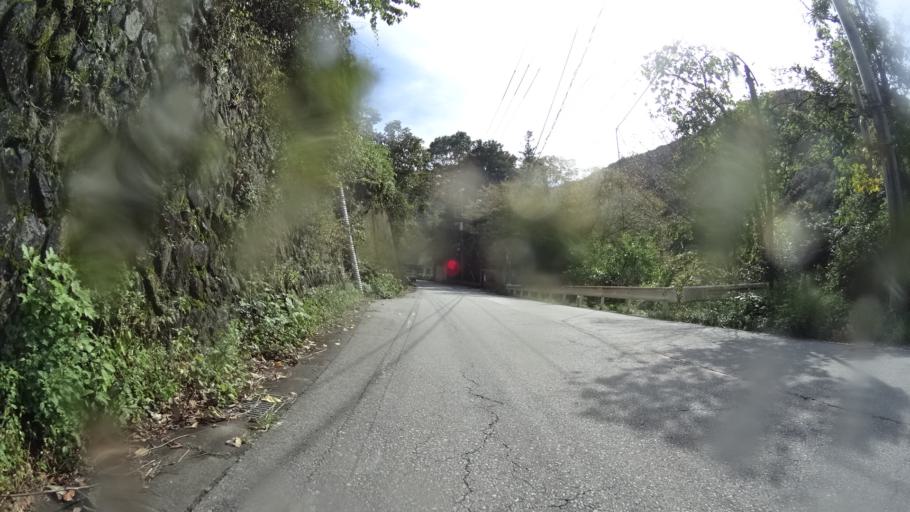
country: JP
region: Yamanashi
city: Otsuki
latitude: 35.7924
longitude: 138.9163
